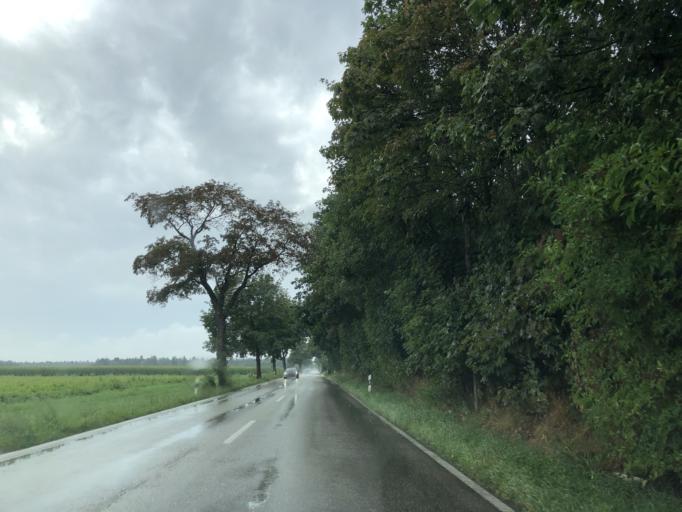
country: DE
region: Bavaria
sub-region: Upper Bavaria
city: Eching
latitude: 48.2861
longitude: 11.6129
